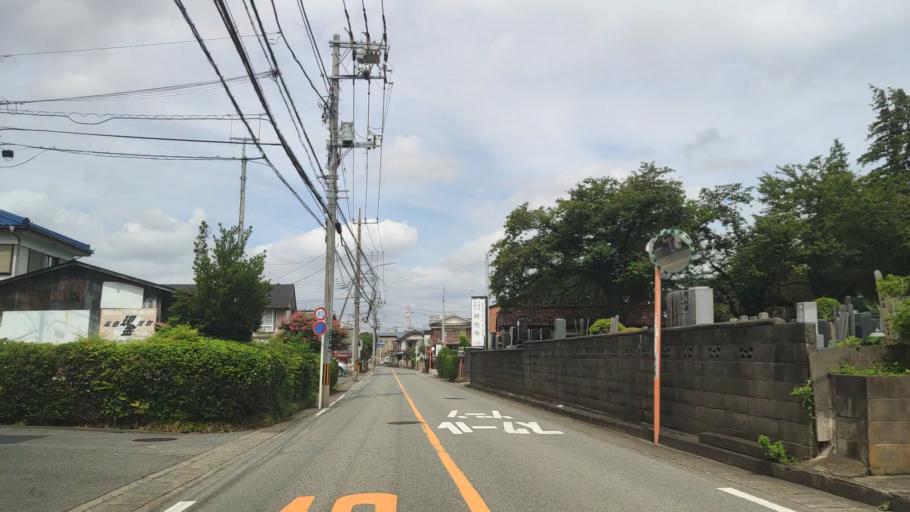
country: JP
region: Kanagawa
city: Minami-rinkan
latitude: 35.4882
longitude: 139.4729
